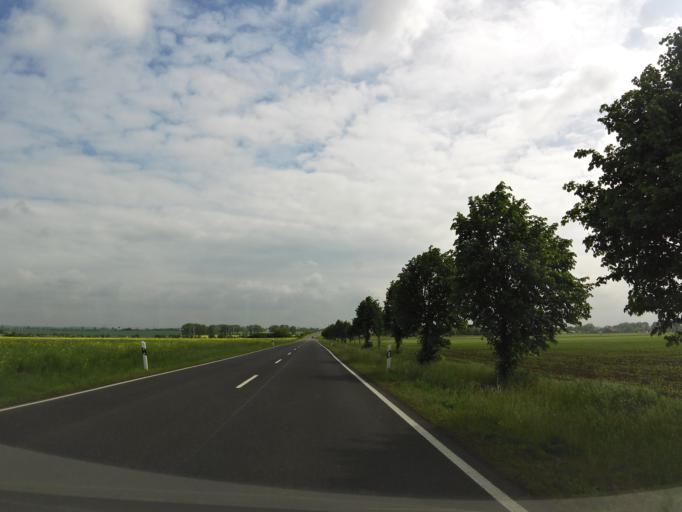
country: DE
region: Thuringia
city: Seebergen
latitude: 50.9195
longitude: 10.8152
